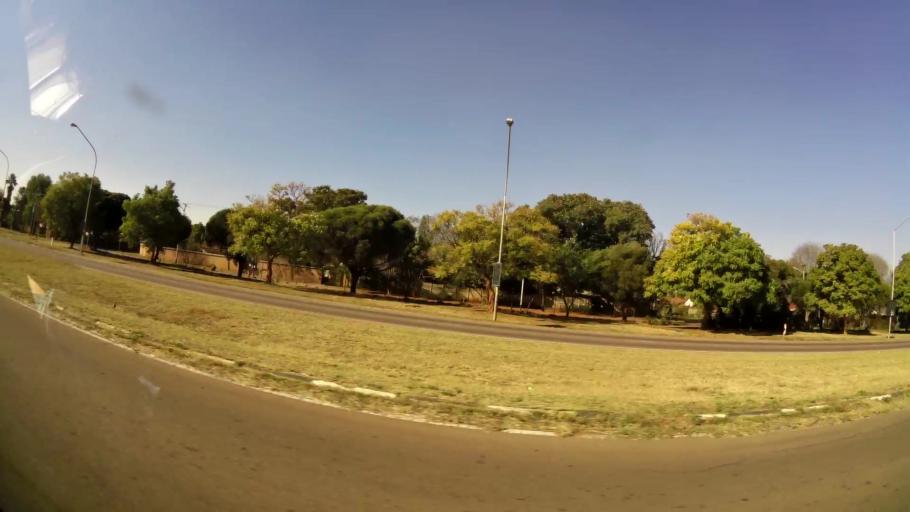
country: ZA
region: Gauteng
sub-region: City of Tshwane Metropolitan Municipality
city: Pretoria
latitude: -25.7172
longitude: 28.2577
